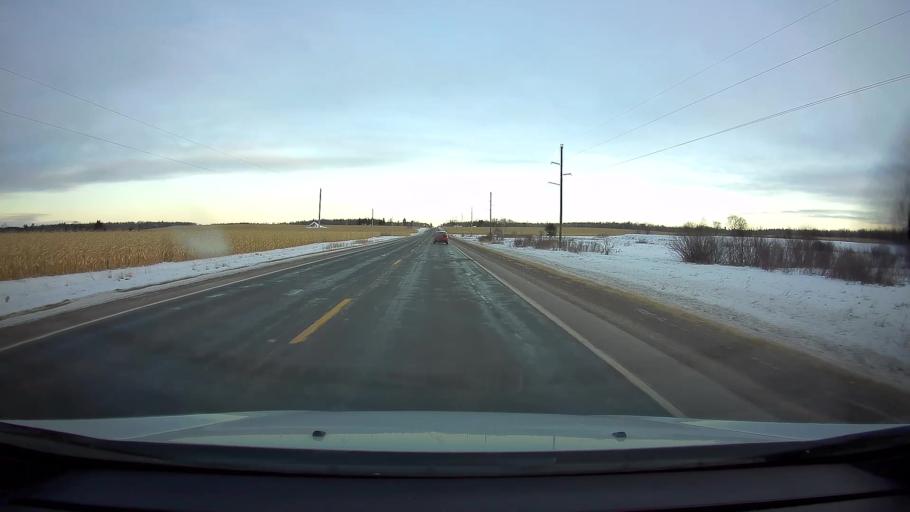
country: US
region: Wisconsin
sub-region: Barron County
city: Turtle Lake
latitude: 45.3444
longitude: -92.1676
